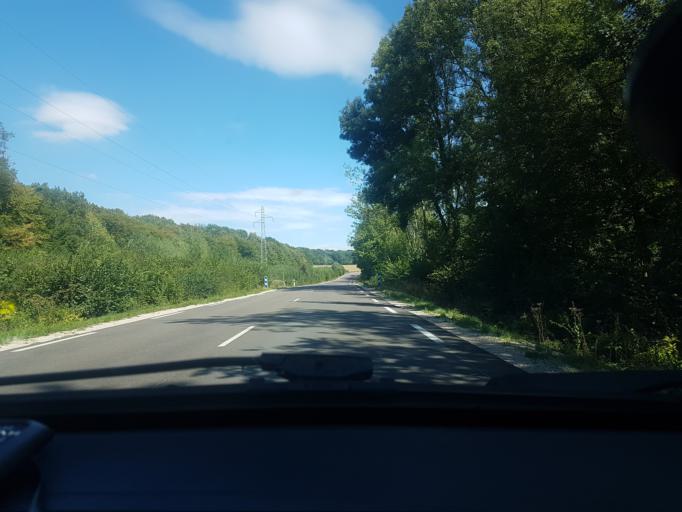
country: FR
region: Franche-Comte
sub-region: Departement de la Haute-Saone
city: Gray-la-Ville
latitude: 47.4098
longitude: 5.4971
